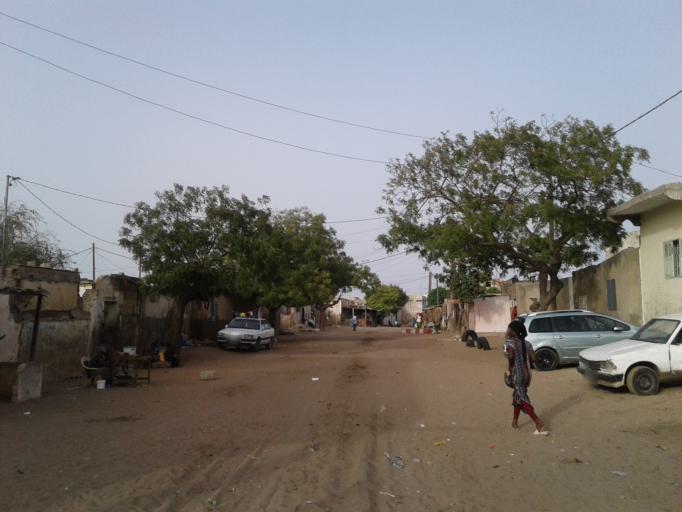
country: SN
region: Dakar
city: Pikine
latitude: 14.7666
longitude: -17.3787
